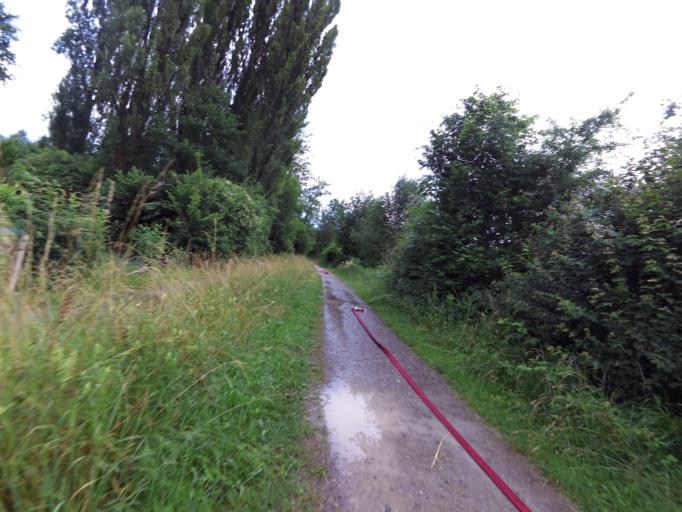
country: CH
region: Zurich
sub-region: Bezirk Dietikon
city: Dietikon / Guggenbuehl
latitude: 47.4041
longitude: 8.4079
